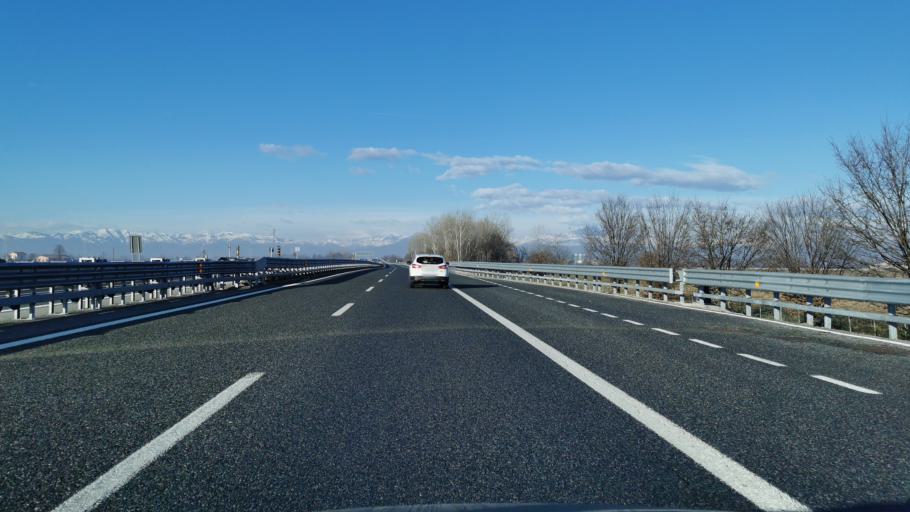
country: IT
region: Piedmont
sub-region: Provincia di Cuneo
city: Trinita
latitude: 44.4690
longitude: 7.7615
